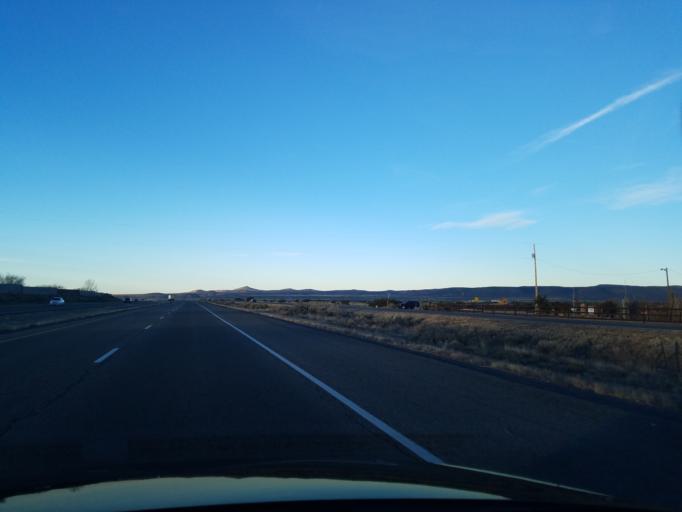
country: US
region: New Mexico
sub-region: Santa Fe County
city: Agua Fria
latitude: 35.6521
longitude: -106.0457
